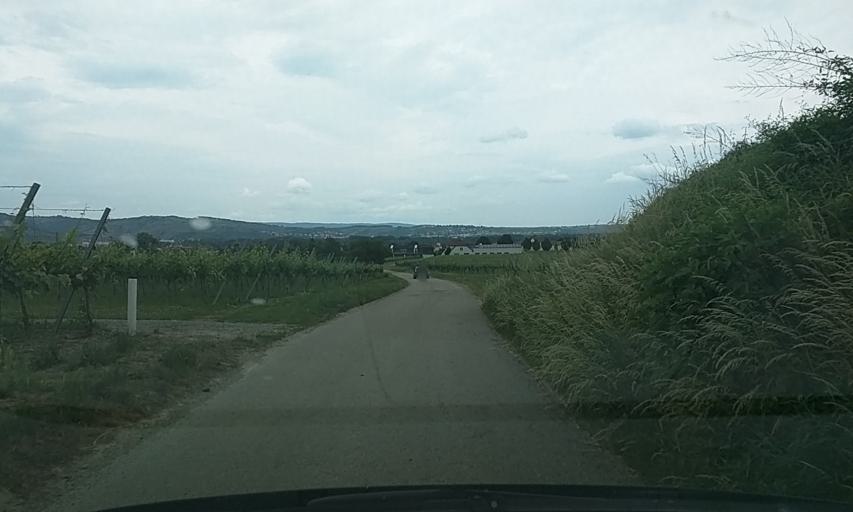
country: AT
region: Lower Austria
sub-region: Politischer Bezirk Krems
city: Weinzierl bei Krems
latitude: 48.3793
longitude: 15.6156
